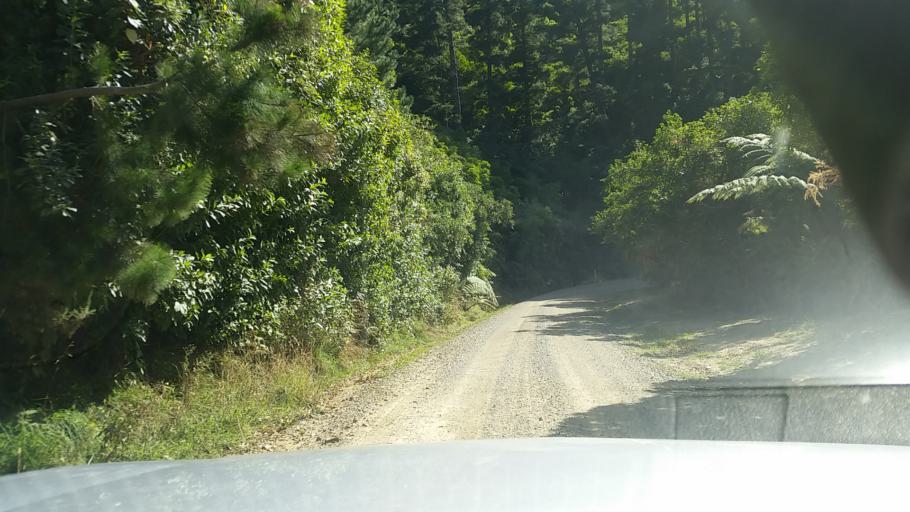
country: NZ
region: Marlborough
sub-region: Marlborough District
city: Picton
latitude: -41.2891
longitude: 174.1712
